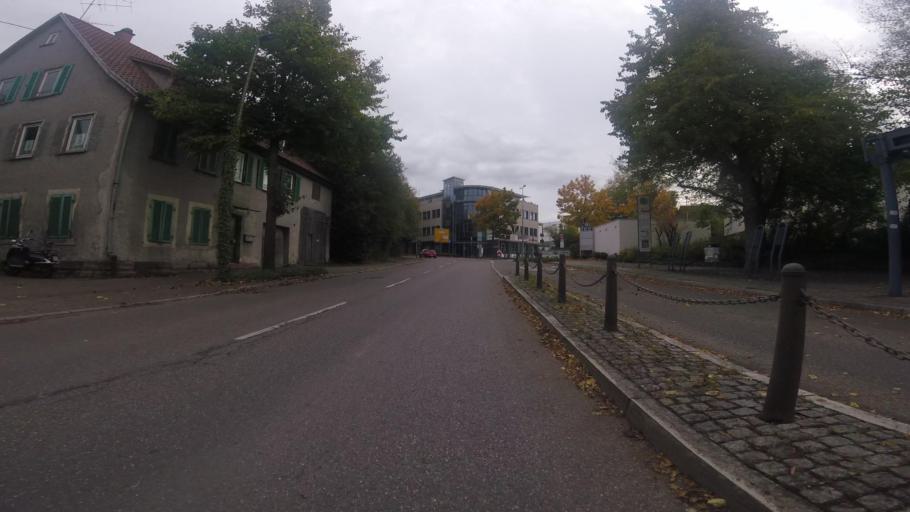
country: DE
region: Baden-Wuerttemberg
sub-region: Regierungsbezirk Stuttgart
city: Backnang
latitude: 48.9438
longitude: 9.4350
